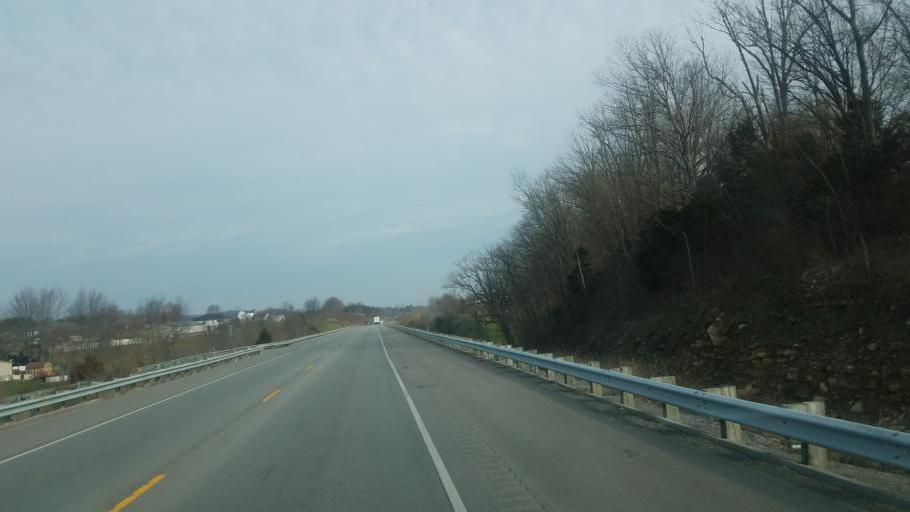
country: US
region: Kentucky
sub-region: Boyle County
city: Junction City
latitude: 37.5296
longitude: -84.8052
